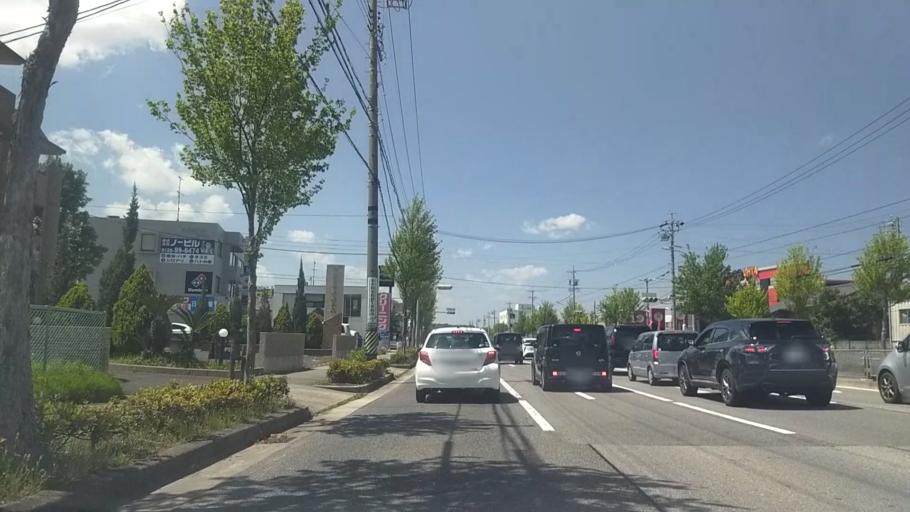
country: JP
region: Aichi
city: Okazaki
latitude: 34.9595
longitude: 137.1885
